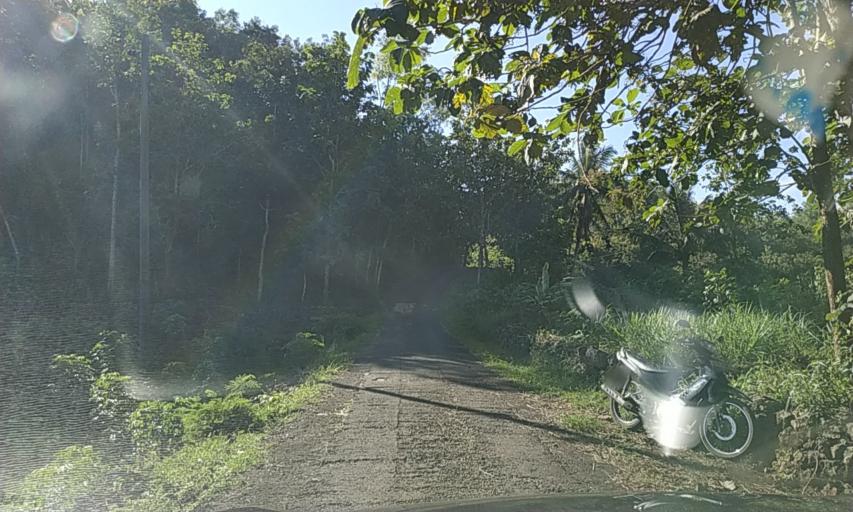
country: ID
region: East Java
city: Krajan
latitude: -8.1327
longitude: 110.9038
